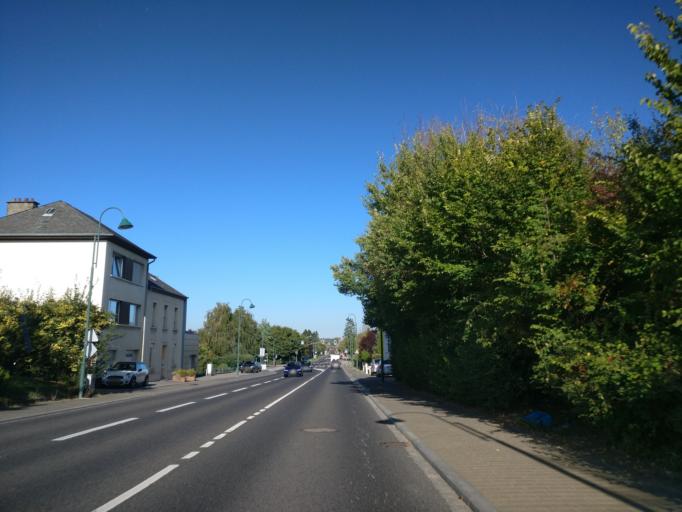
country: LU
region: Luxembourg
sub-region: Canton de Capellen
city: Mamer
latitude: 49.6332
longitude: 6.0185
